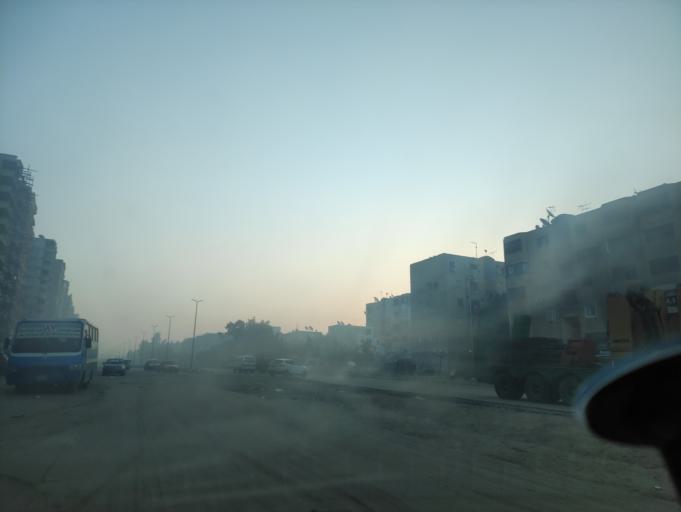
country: EG
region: Muhafazat al Qahirah
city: Cairo
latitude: 30.0483
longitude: 31.3688
